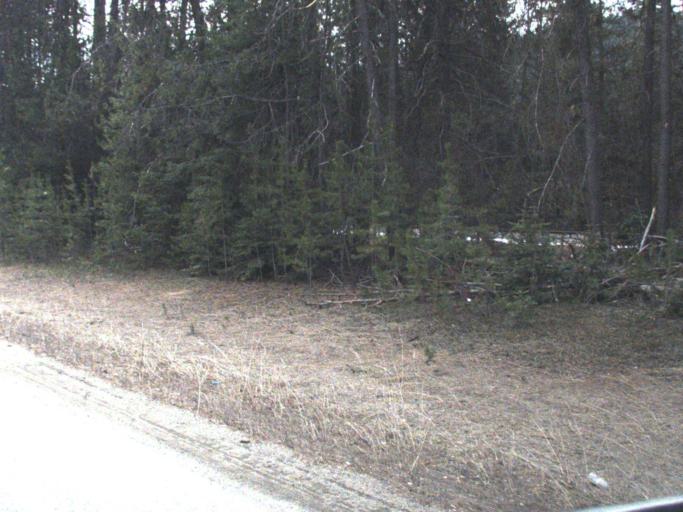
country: US
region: Washington
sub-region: Pend Oreille County
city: Newport
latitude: 48.2640
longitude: -117.2557
